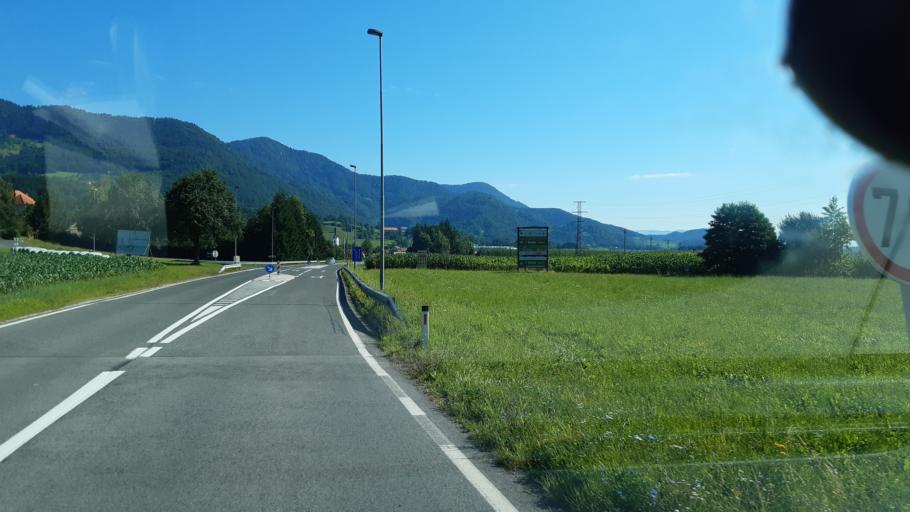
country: SI
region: Vransko
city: Vransko
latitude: 46.2383
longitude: 14.9482
